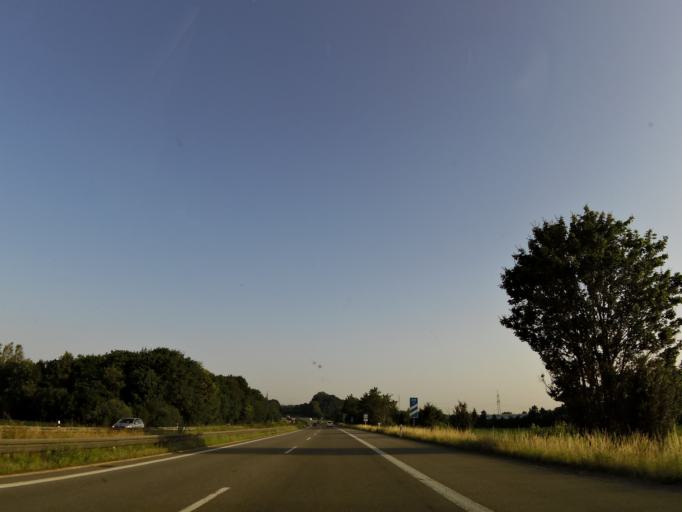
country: DE
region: Bavaria
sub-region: Swabia
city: Memmingen
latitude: 47.9596
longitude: 10.1877
